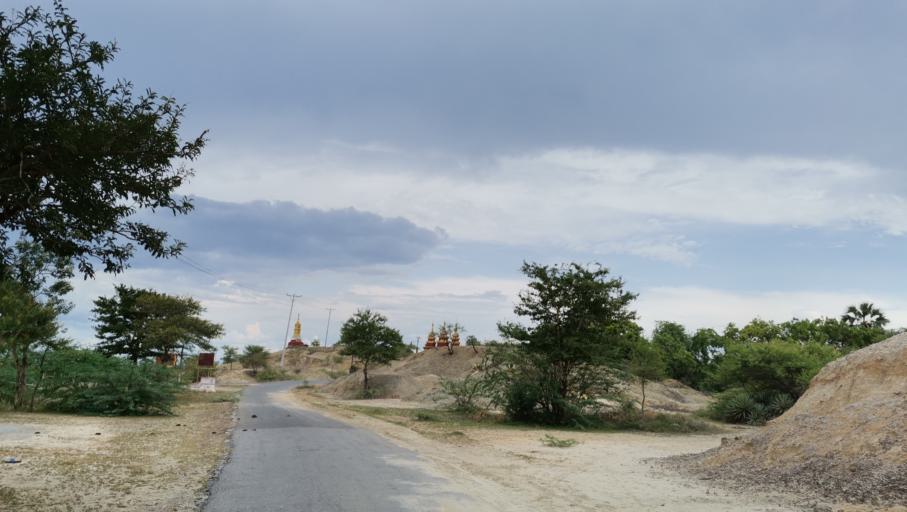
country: MM
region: Mandalay
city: Myingyan
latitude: 21.8204
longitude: 95.3968
